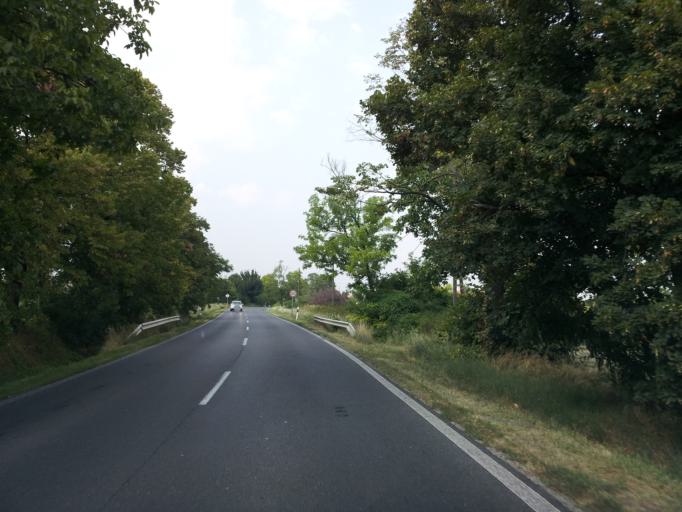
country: HU
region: Gyor-Moson-Sopron
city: Nyul
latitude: 47.5754
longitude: 17.6975
